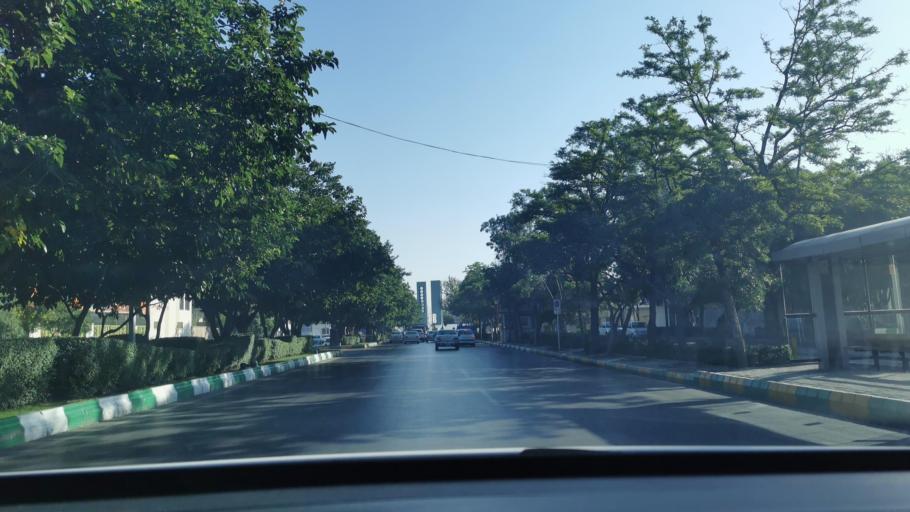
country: IR
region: Razavi Khorasan
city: Mashhad
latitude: 36.2986
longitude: 59.5626
